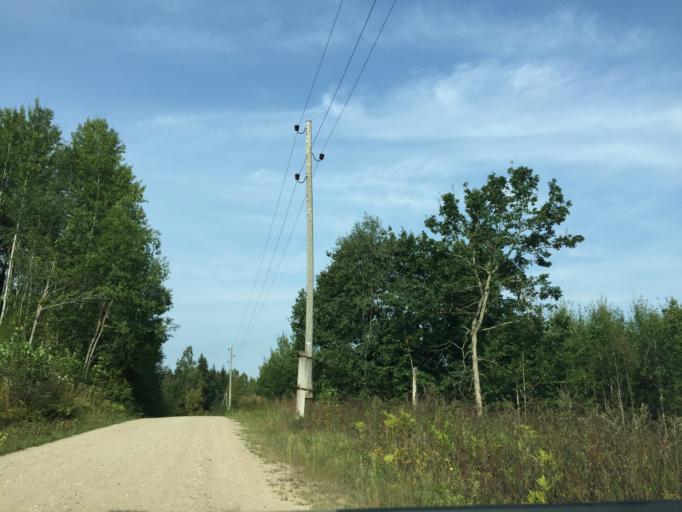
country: LV
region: Dagda
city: Dagda
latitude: 56.2645
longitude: 27.6437
